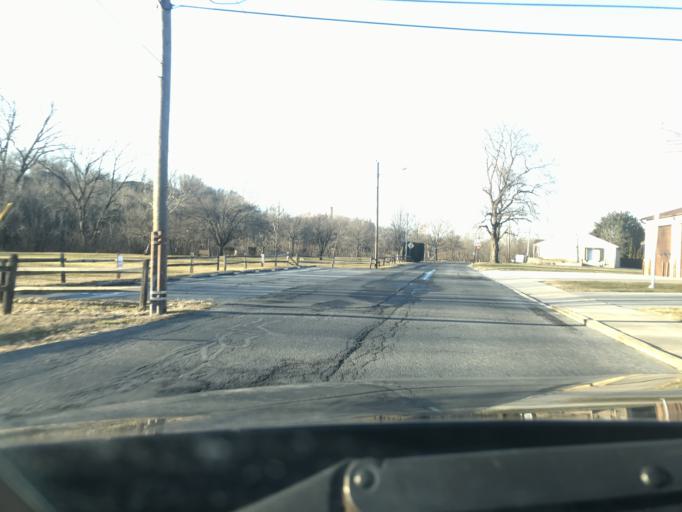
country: US
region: Pennsylvania
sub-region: Northampton County
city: Northampton
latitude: 40.6812
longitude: -75.4977
